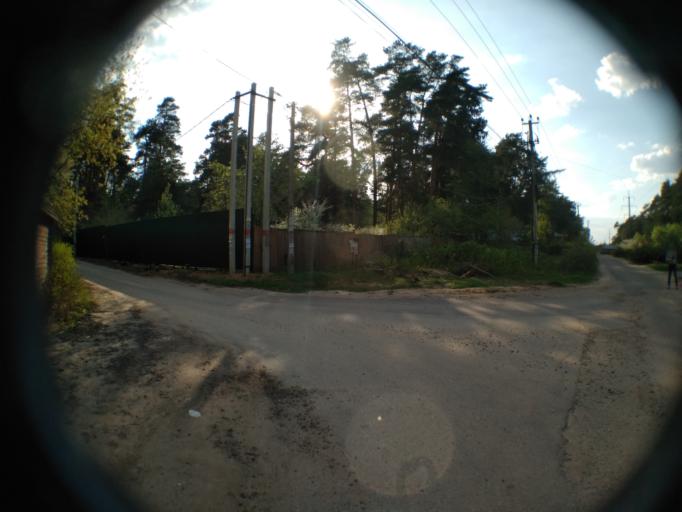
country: RU
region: Moskovskaya
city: Kratovo
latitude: 55.5799
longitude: 38.1658
